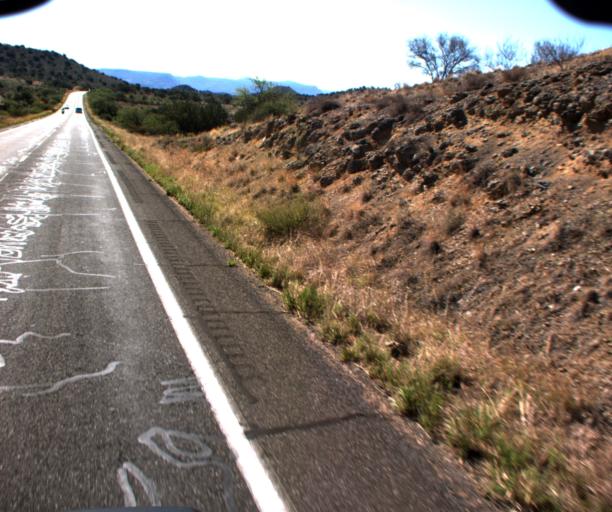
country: US
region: Arizona
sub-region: Yavapai County
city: Lake Montezuma
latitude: 34.6970
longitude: -111.7586
